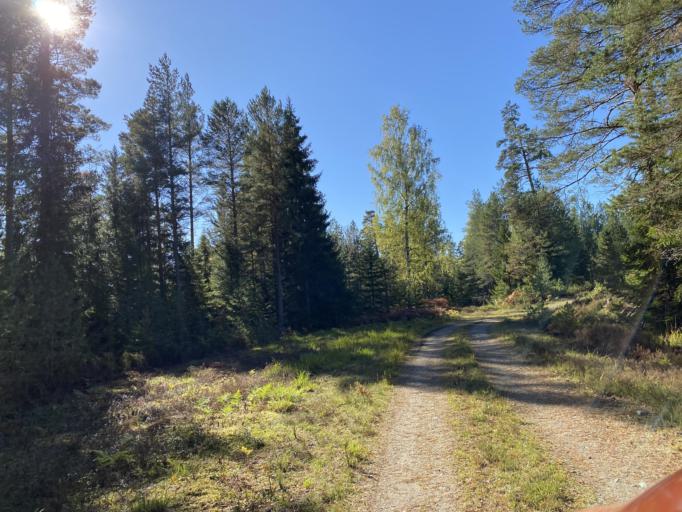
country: SE
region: OErebro
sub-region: Orebro Kommun
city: Odensbacken
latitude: 58.9733
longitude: 15.6207
